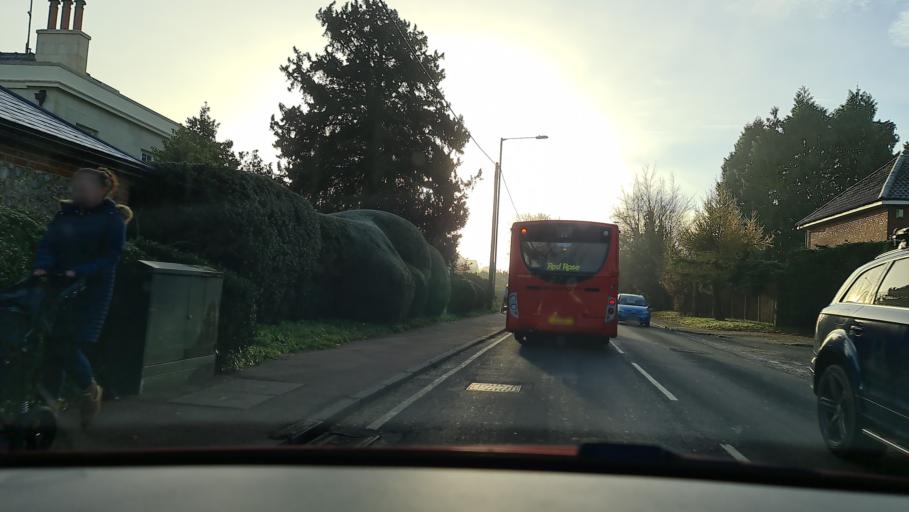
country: GB
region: England
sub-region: Buckinghamshire
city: Wendover
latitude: 51.7695
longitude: -0.7462
